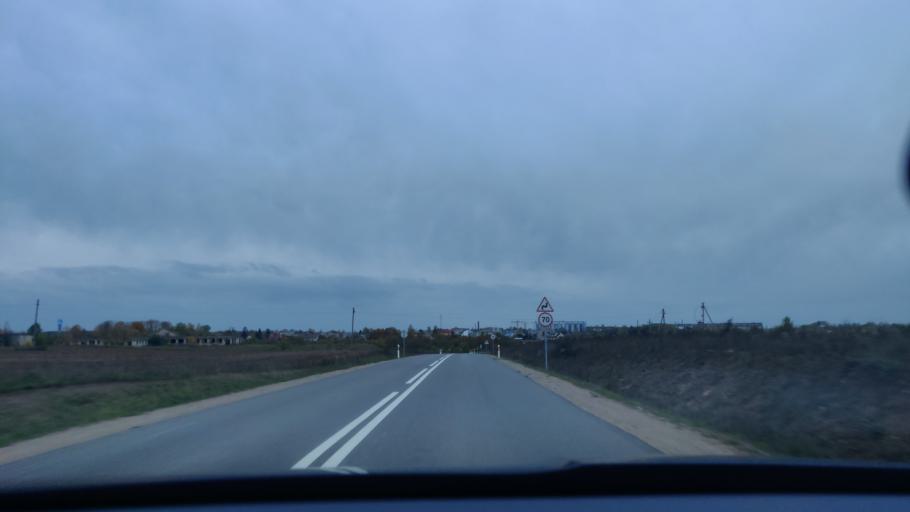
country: LT
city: Lentvaris
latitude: 54.6066
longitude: 24.9968
